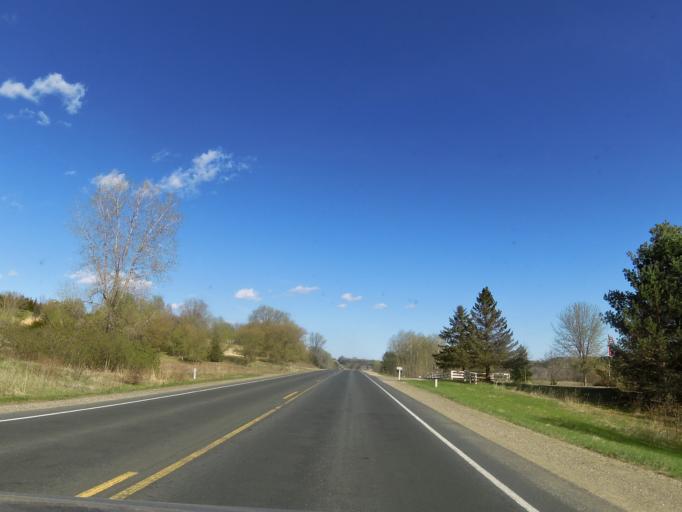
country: US
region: Wisconsin
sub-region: Saint Croix County
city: North Hudson
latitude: 45.0486
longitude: -92.7137
